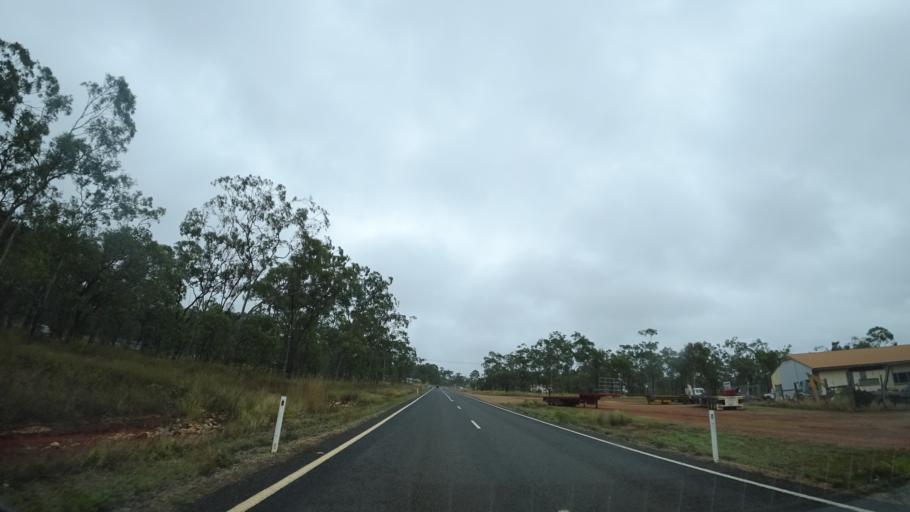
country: AU
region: Queensland
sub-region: Tablelands
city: Ravenshoe
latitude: -17.6818
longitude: 145.1274
